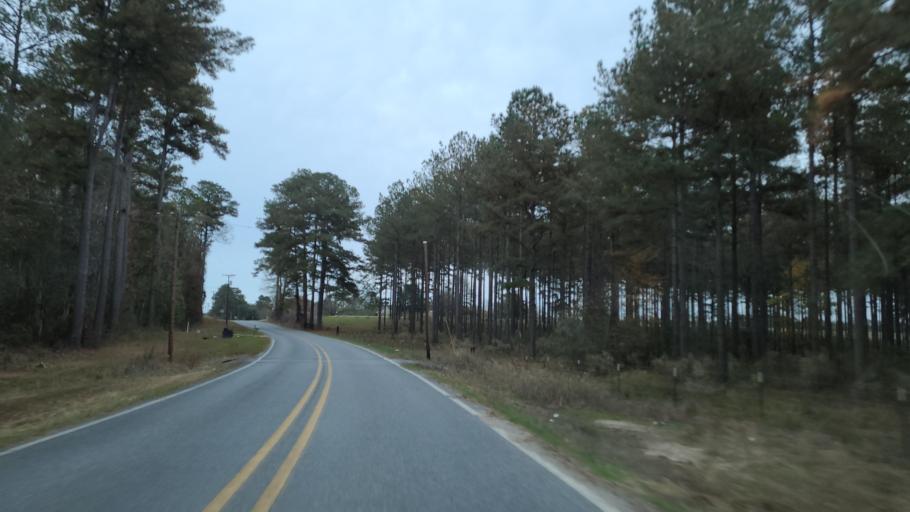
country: US
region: Mississippi
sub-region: Clarke County
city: Quitman
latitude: 32.0289
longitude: -88.8178
